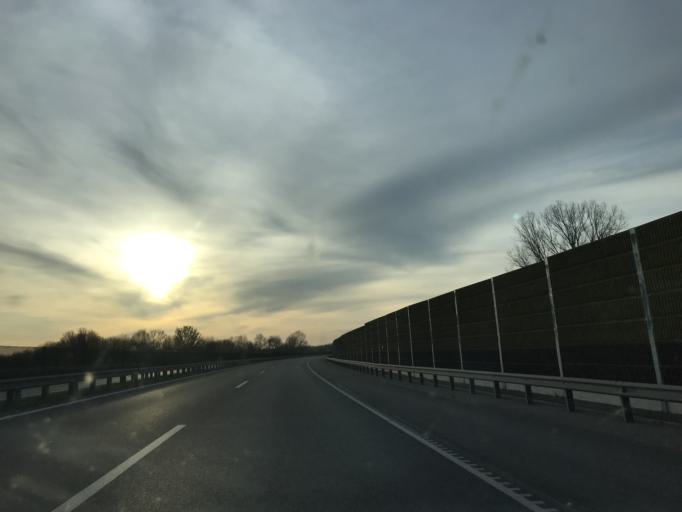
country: HU
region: Pest
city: Peteri
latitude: 47.3714
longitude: 19.4150
